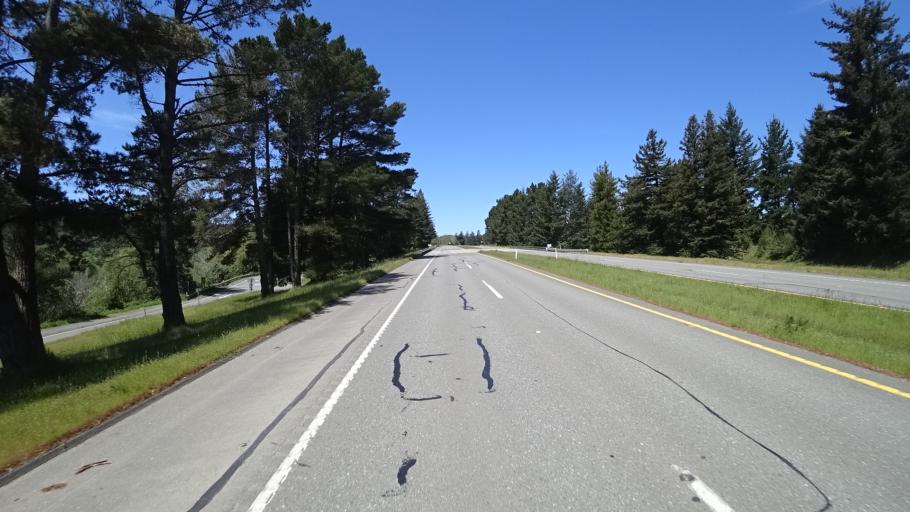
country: US
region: California
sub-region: Humboldt County
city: Blue Lake
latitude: 40.8977
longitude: -124.0201
